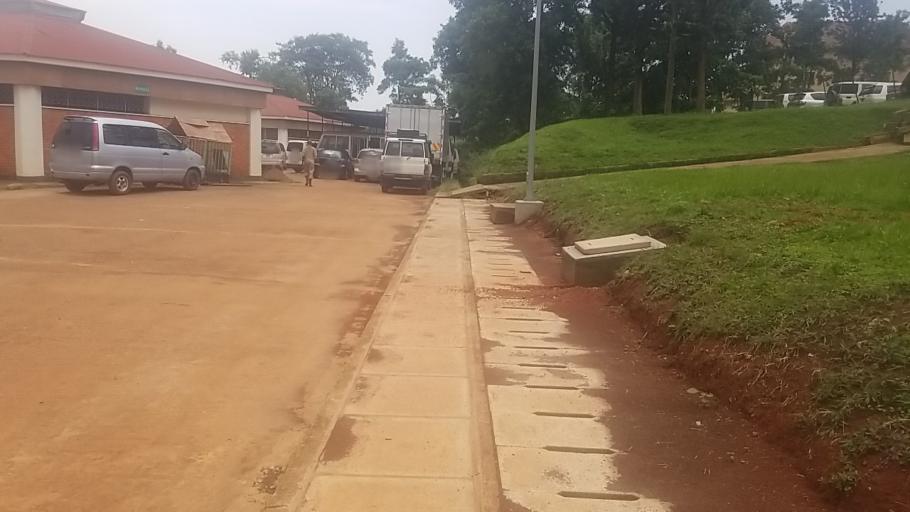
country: UG
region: Central Region
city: Kampala Central Division
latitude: 0.3402
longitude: 32.5682
